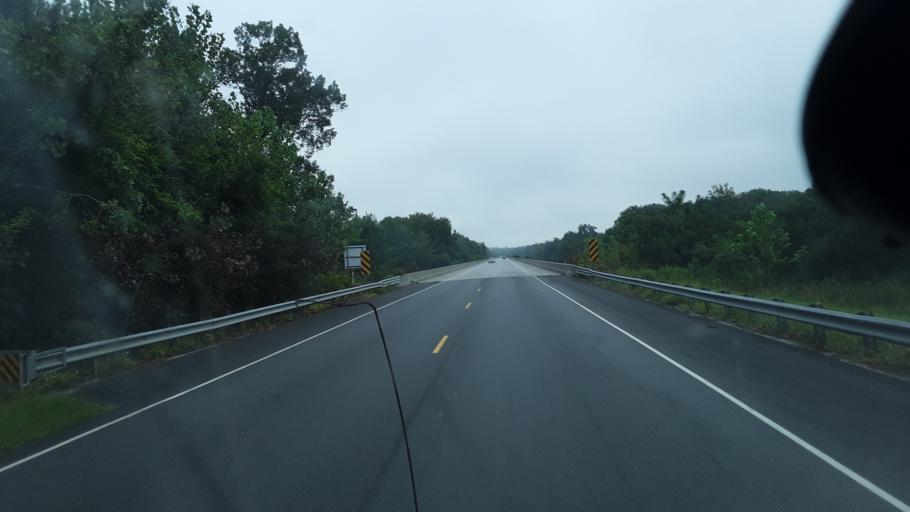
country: US
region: South Carolina
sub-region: Florence County
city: Johnsonville
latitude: 33.9026
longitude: -79.4373
